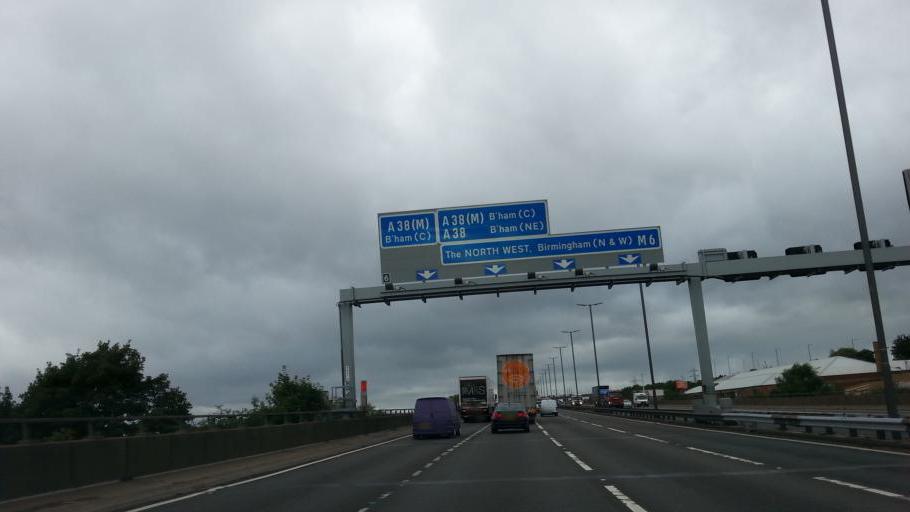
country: GB
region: England
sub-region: City and Borough of Birmingham
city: Birmingham
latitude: 52.5065
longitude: -1.8541
